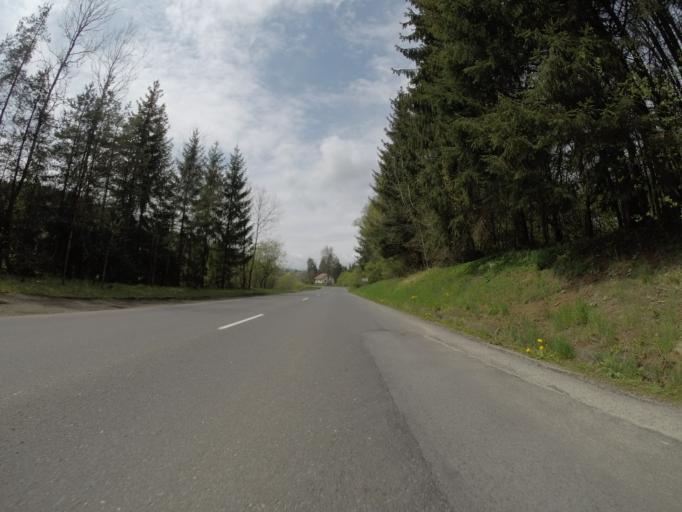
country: SK
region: Banskobystricky
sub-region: Okres Banska Bystrica
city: Brezno
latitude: 48.8231
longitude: 19.6934
